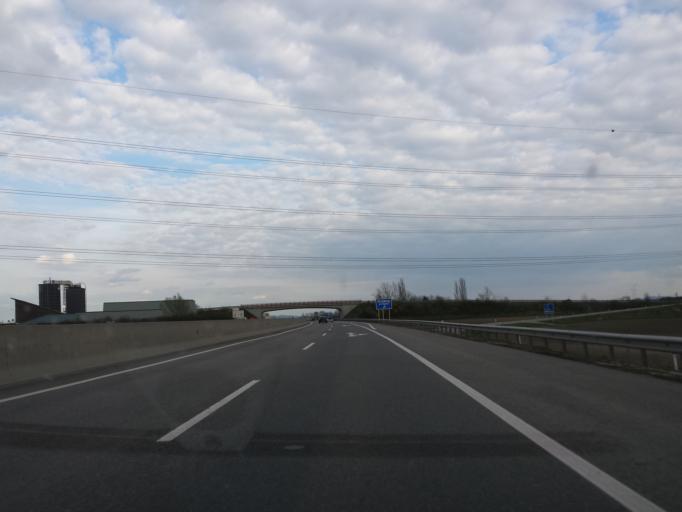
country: AT
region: Lower Austria
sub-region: Politischer Bezirk Tulln
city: Kirchberg am Wagram
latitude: 48.4075
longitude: 15.8775
